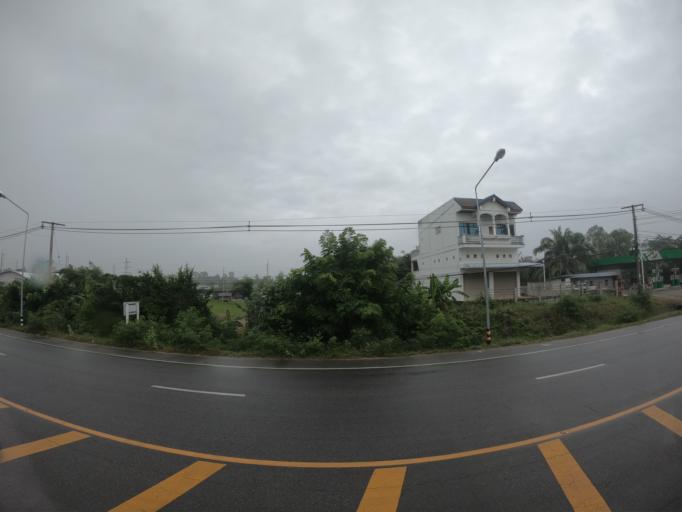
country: TH
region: Maha Sarakham
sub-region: Amphoe Borabue
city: Borabue
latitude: 16.0470
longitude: 103.1028
